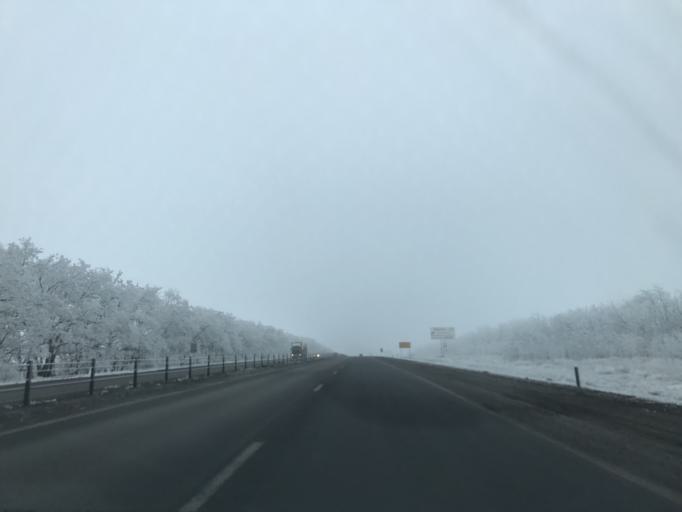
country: RU
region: Rostov
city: Likhoy
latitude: 48.1722
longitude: 40.2640
